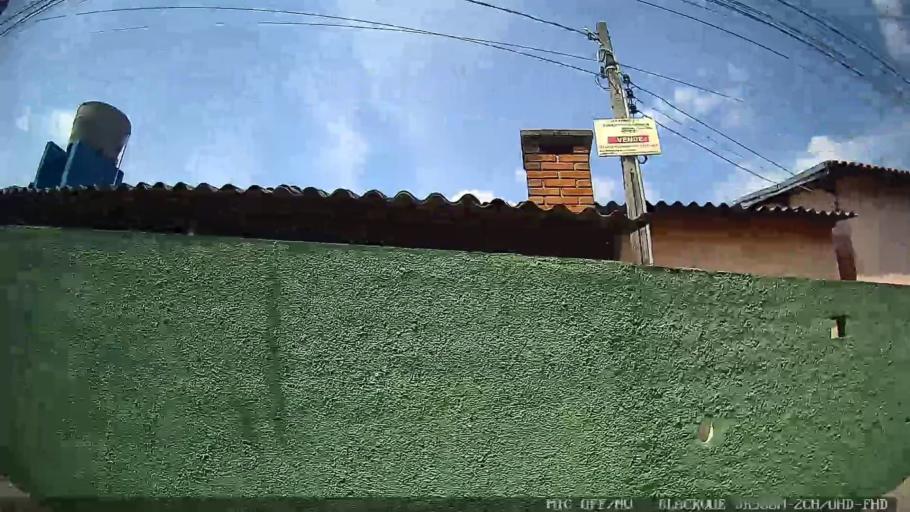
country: BR
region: Sao Paulo
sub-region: Cabreuva
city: Cabreuva
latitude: -23.2547
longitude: -47.0610
